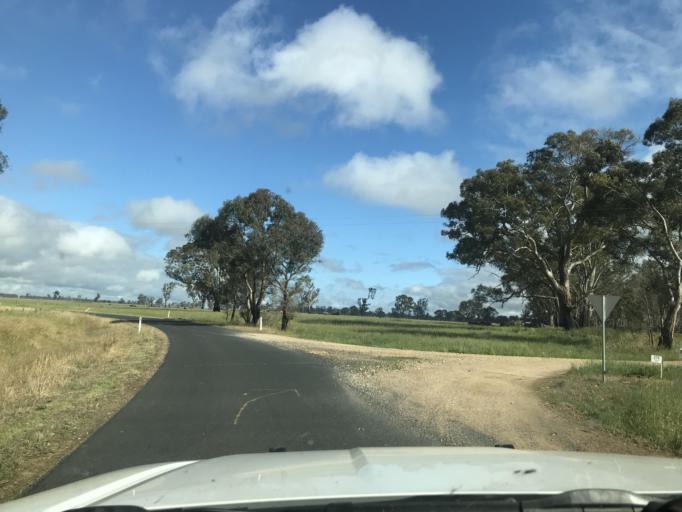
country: AU
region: South Australia
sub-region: Wattle Range
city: Penola
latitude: -37.2114
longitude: 141.1299
